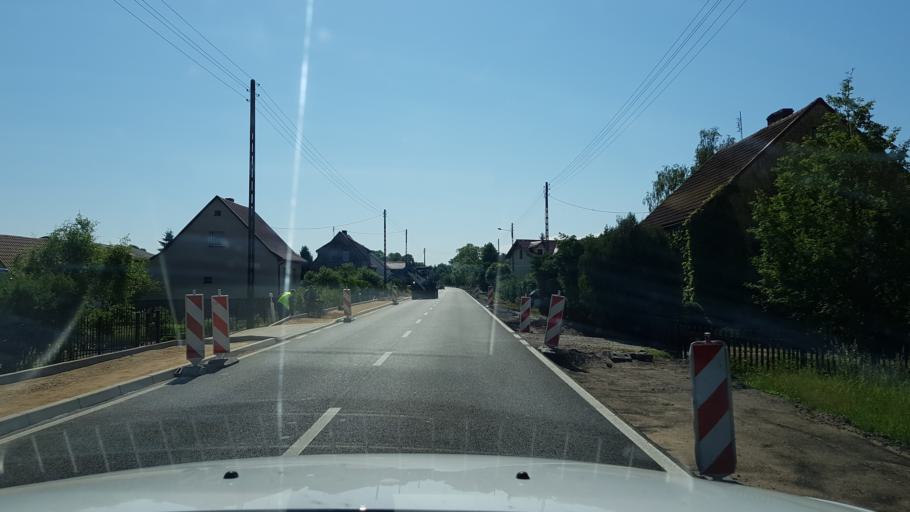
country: PL
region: West Pomeranian Voivodeship
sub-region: Powiat mysliborski
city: Boleszkowice
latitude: 52.6896
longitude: 14.6300
